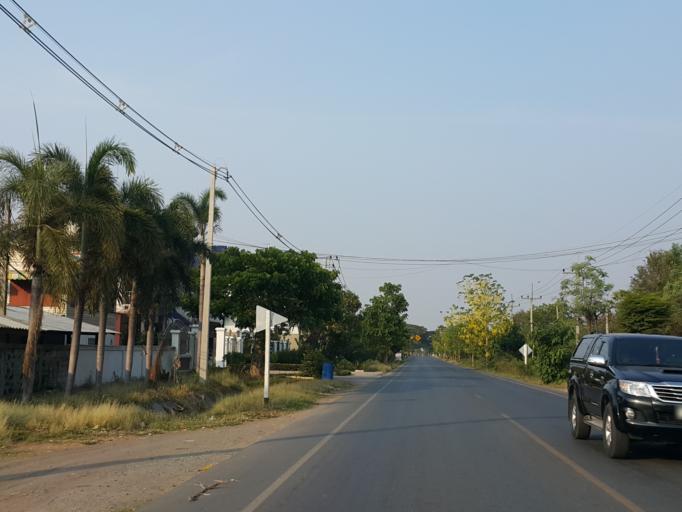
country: TH
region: Chai Nat
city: Sankhaburi
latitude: 15.0659
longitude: 100.1645
